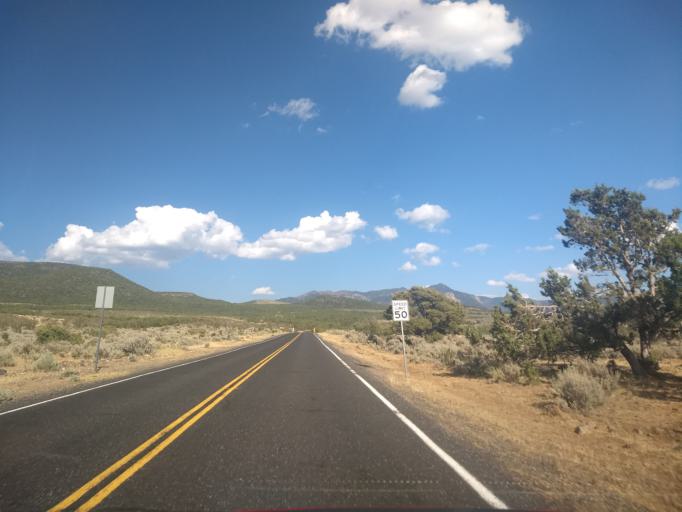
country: US
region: Utah
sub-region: Washington County
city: Enterprise
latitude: 37.4184
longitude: -113.5557
